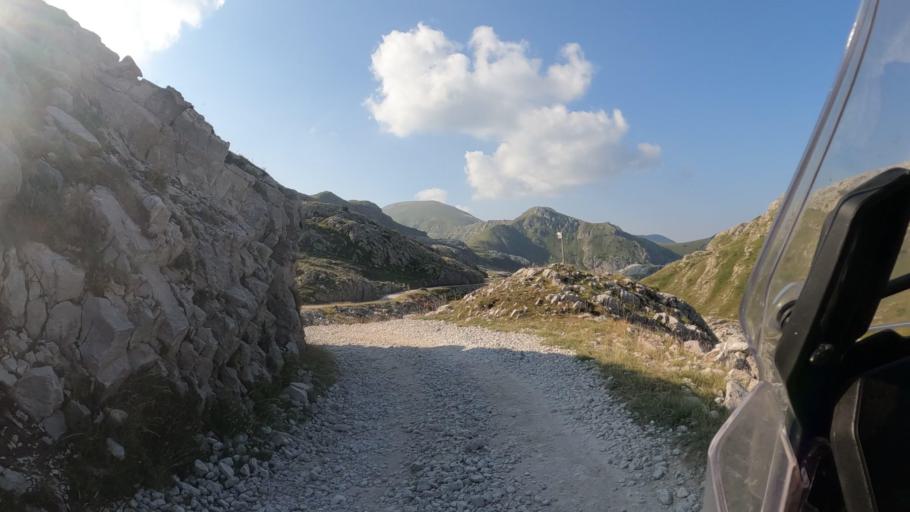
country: IT
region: Piedmont
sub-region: Provincia di Cuneo
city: Limone Piemonte
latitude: 44.1684
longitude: 7.6674
